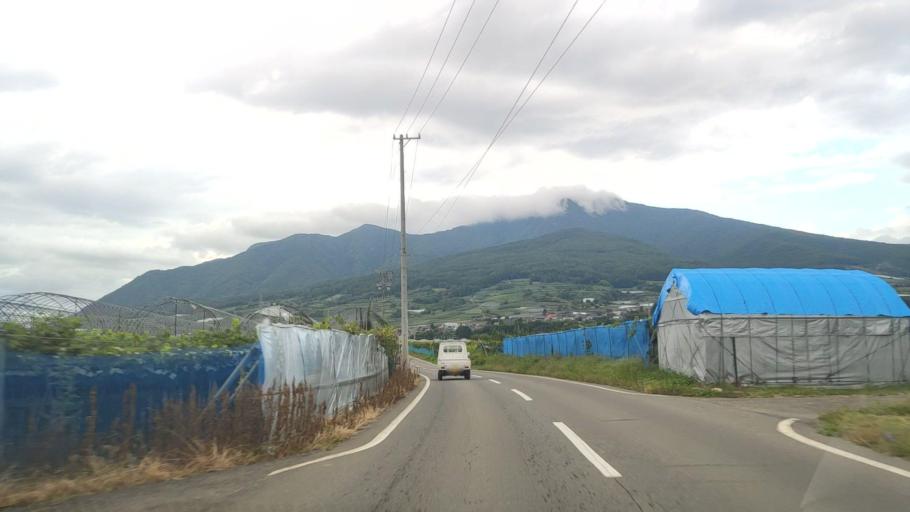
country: JP
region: Nagano
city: Nakano
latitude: 36.7679
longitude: 138.3735
